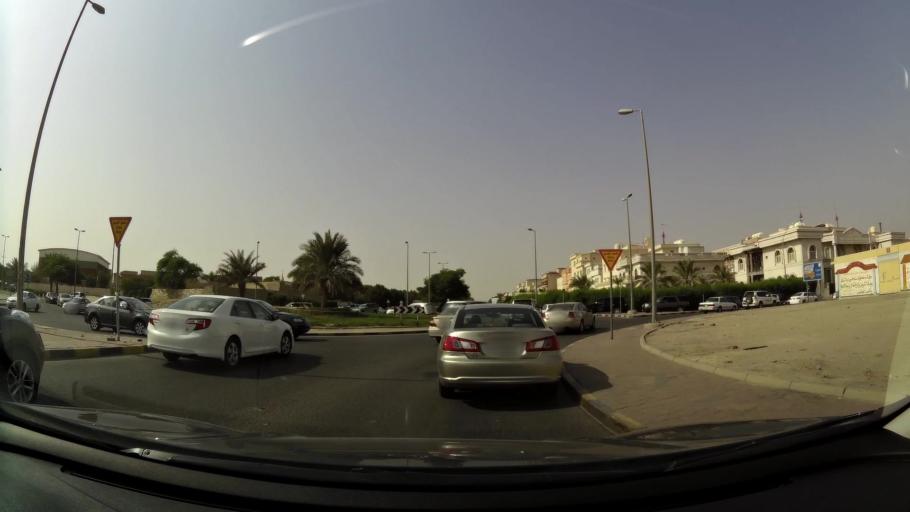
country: KW
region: Muhafazat al Jahra'
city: Al Jahra'
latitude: 29.3436
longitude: 47.6659
